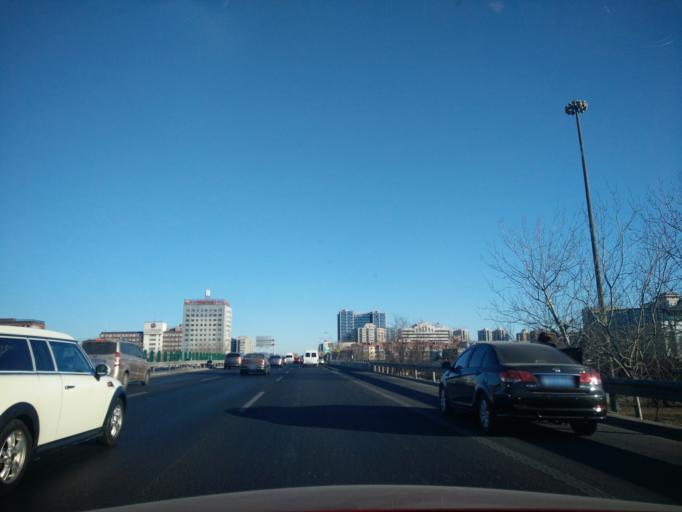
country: CN
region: Beijing
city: Lugu
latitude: 39.8946
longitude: 116.2052
